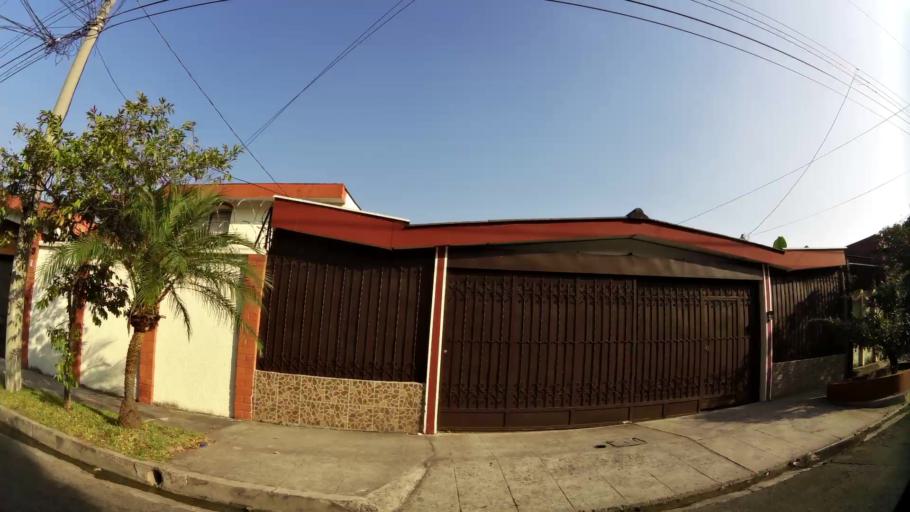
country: SV
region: La Libertad
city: Antiguo Cuscatlan
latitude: 13.6776
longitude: -89.2251
